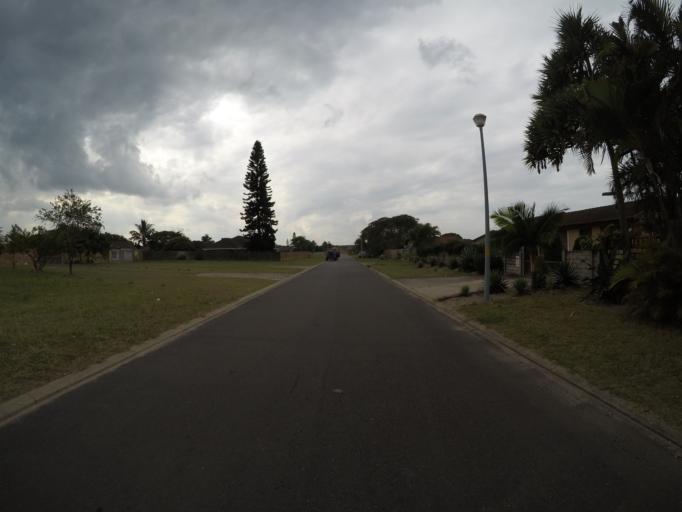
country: ZA
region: KwaZulu-Natal
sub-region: uThungulu District Municipality
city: Richards Bay
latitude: -28.7361
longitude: 32.0507
